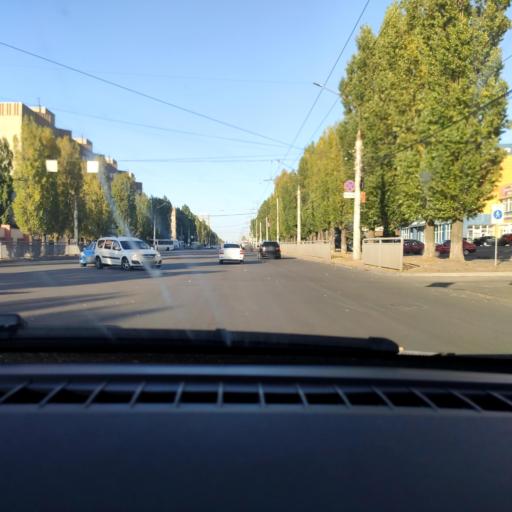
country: RU
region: Voronezj
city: Voronezh
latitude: 51.6931
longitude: 39.2691
